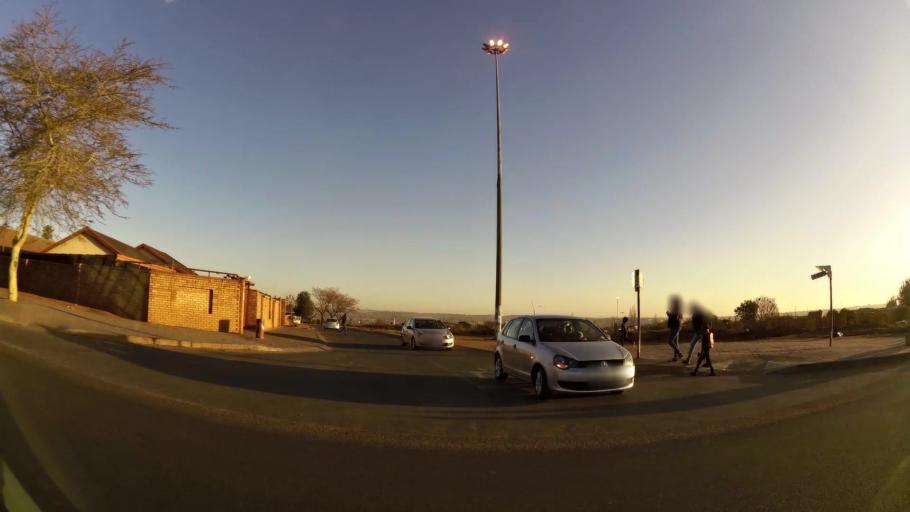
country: ZA
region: Gauteng
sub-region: Ekurhuleni Metropolitan Municipality
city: Tembisa
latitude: -26.0078
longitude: 28.2154
